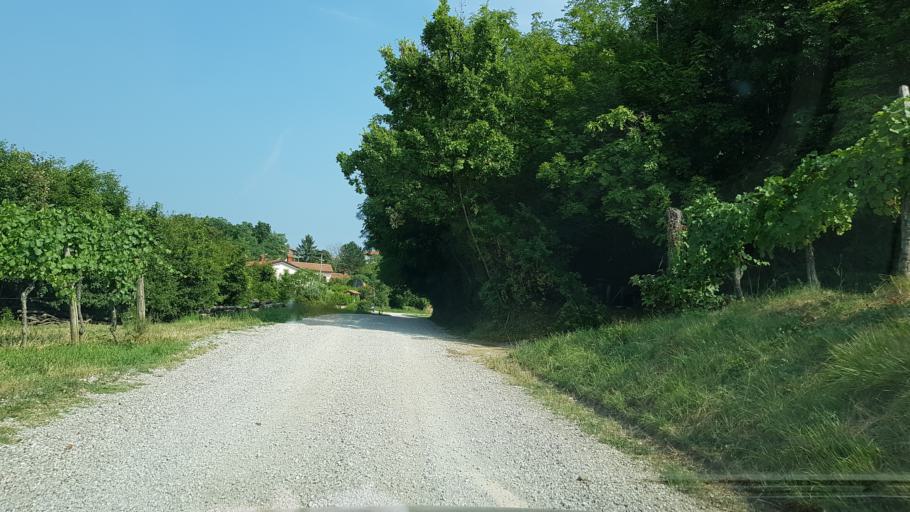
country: SI
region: Brda
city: Dobrovo
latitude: 45.9933
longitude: 13.5171
